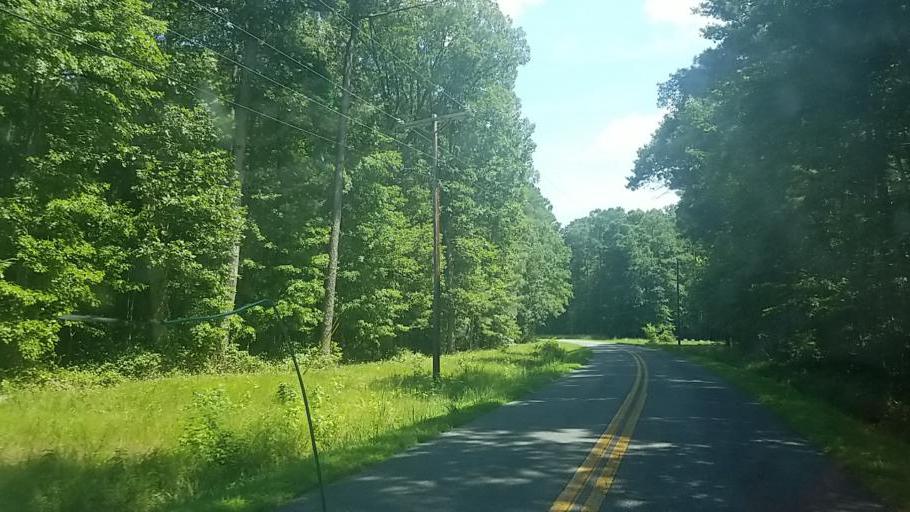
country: US
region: Maryland
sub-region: Wicomico County
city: Hebron
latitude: 38.4242
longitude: -75.8745
